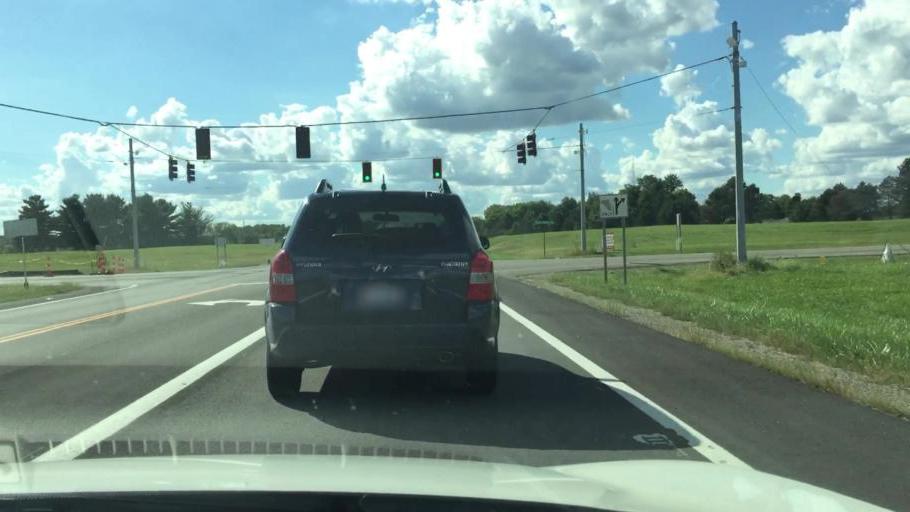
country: US
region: Ohio
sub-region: Clark County
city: Northridge
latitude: 39.9774
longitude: -83.7644
